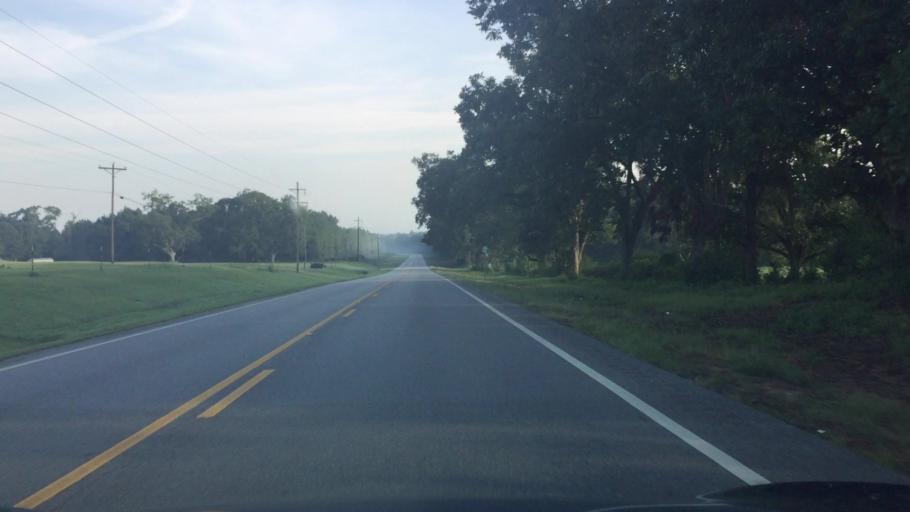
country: US
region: Alabama
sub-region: Covington County
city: Florala
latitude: 31.0504
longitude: -86.3878
